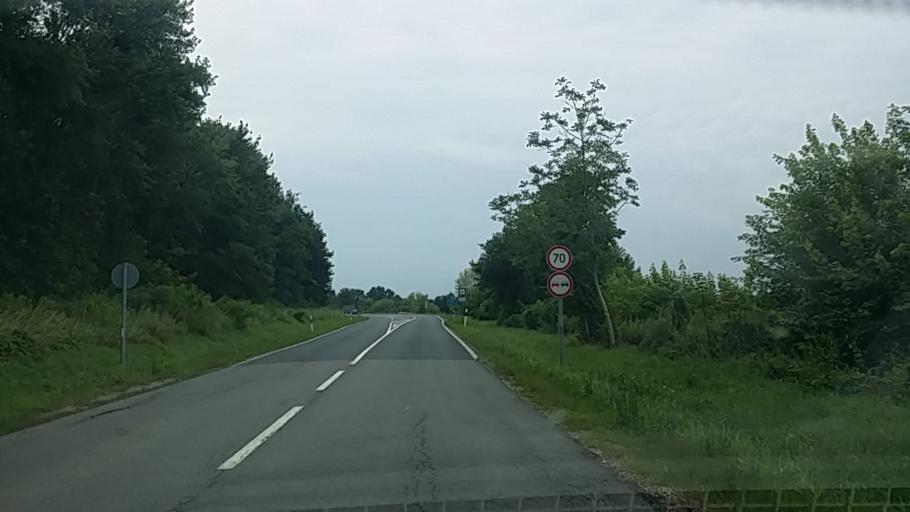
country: HR
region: Medimurska
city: Domasinec
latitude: 46.4773
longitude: 16.6535
